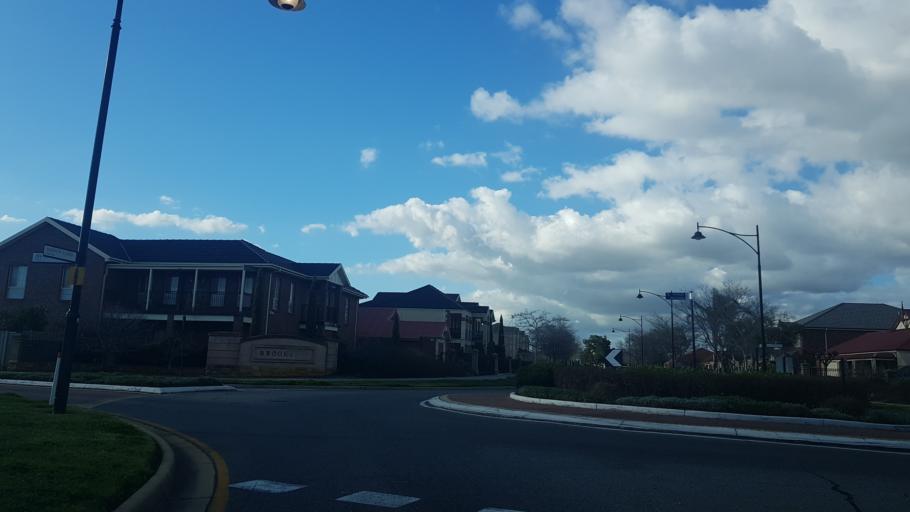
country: AU
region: South Australia
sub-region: Salisbury
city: Ingle Farm
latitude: -34.8125
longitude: 138.6084
